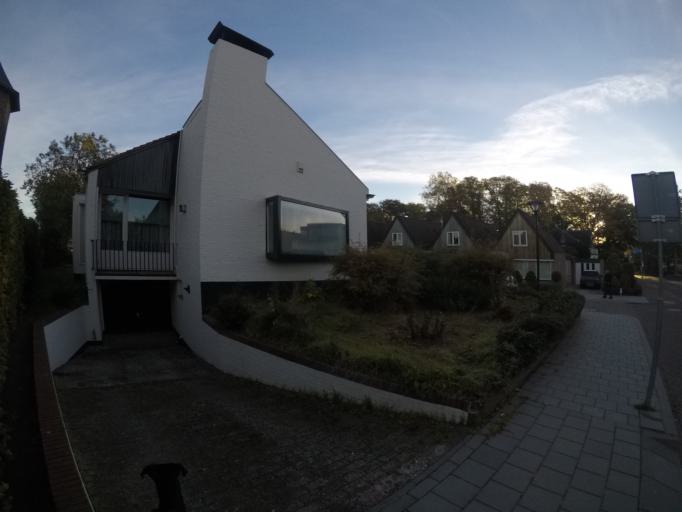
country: NL
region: Gelderland
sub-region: Gemeente Zevenaar
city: Zevenaar
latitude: 51.9288
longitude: 6.0735
